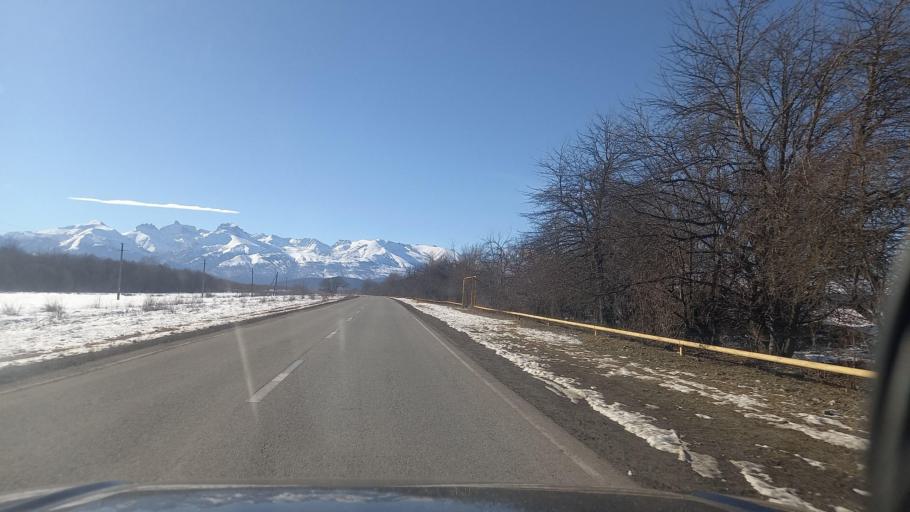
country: RU
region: North Ossetia
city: Chikola
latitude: 43.1752
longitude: 43.8766
